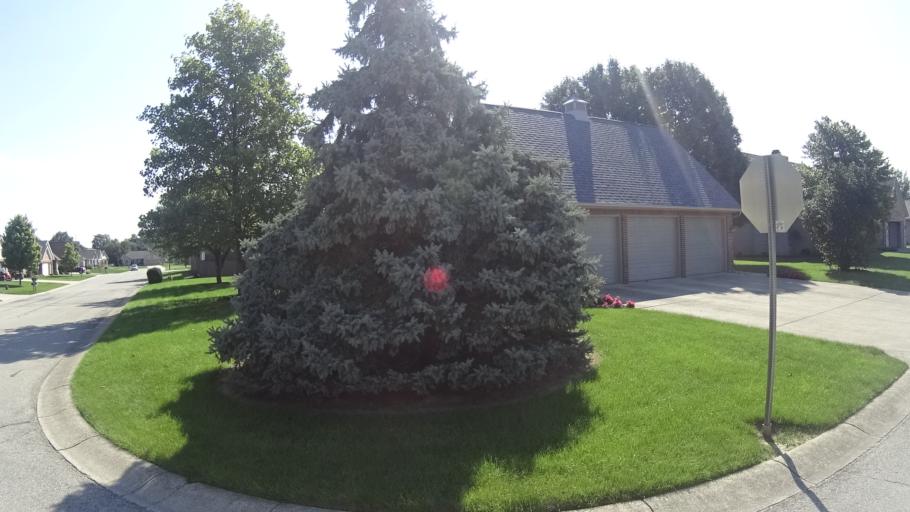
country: US
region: Indiana
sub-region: Madison County
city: Lapel
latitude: 40.0595
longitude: -85.8480
